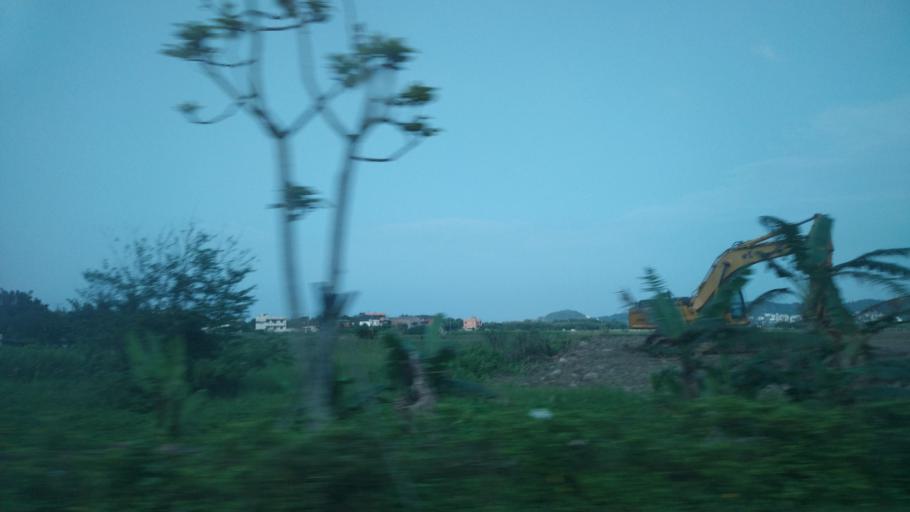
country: TW
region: Taiwan
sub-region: Keelung
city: Keelung
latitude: 25.2340
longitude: 121.6296
